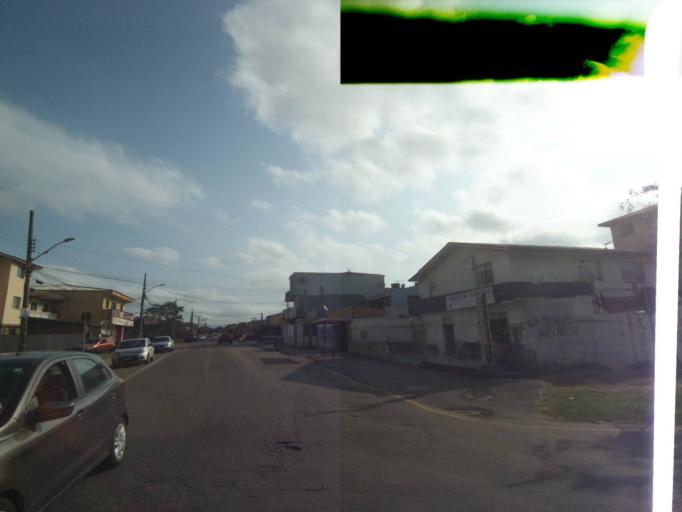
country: BR
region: Parana
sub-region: Sao Jose Dos Pinhais
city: Sao Jose dos Pinhais
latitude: -25.5428
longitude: -49.2574
